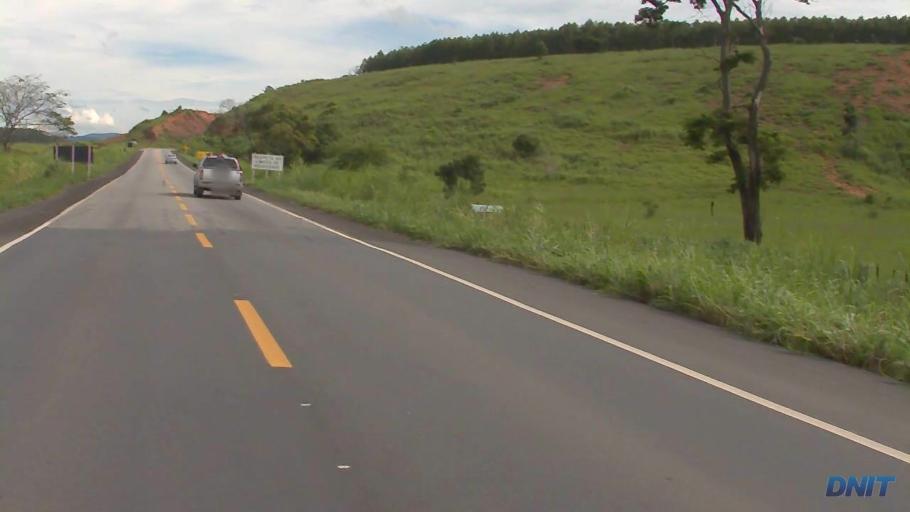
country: BR
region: Minas Gerais
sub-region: Ipaba
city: Ipaba
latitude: -19.2921
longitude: -42.3558
